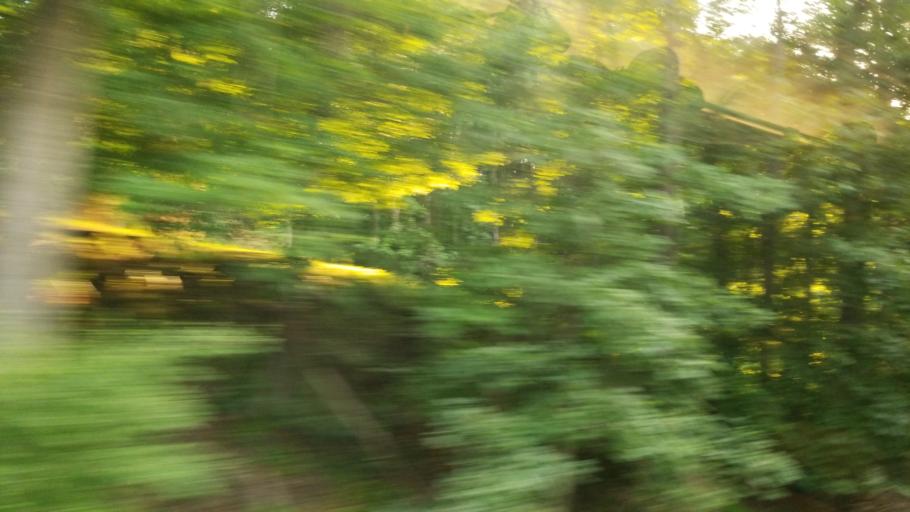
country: US
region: Virginia
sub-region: Prince William County
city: Yorkshire
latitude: 38.7787
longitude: -77.4268
